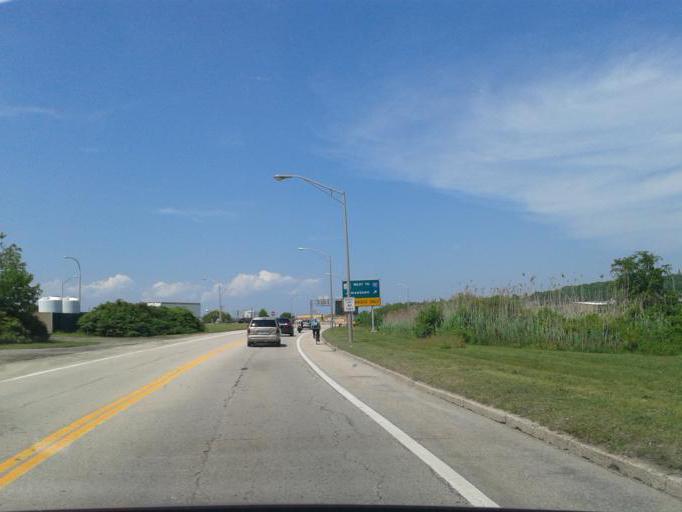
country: US
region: Rhode Island
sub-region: Newport County
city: Newport
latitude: 41.5013
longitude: -71.3174
